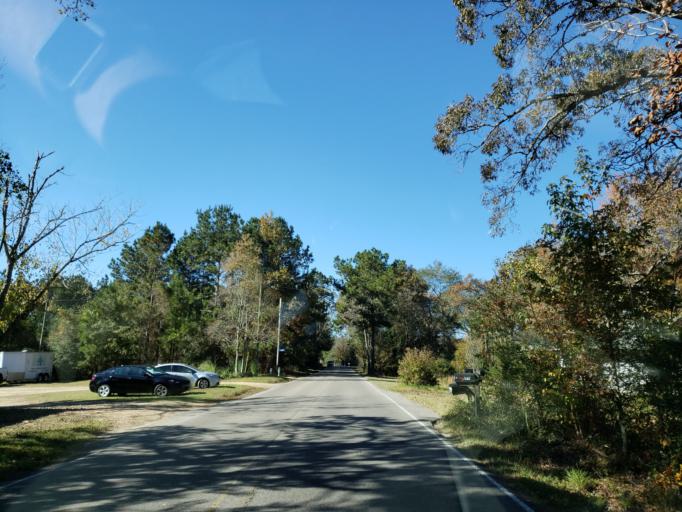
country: US
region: Mississippi
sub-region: Lamar County
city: West Hattiesburg
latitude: 31.3056
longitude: -89.3862
